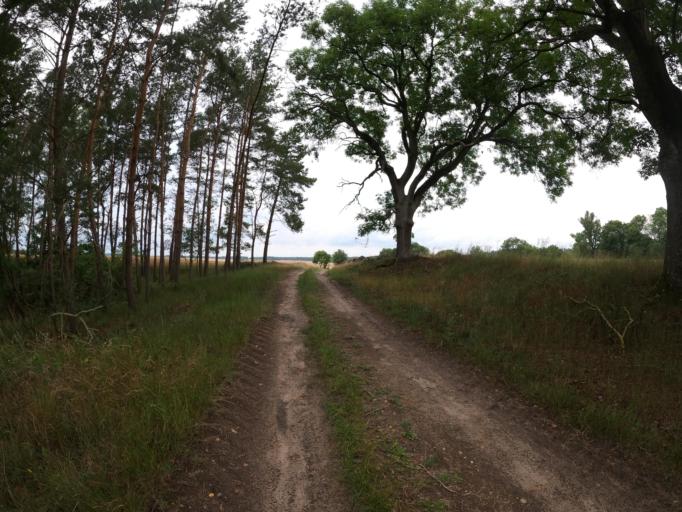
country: DE
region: Brandenburg
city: Althuttendorf
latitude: 53.0273
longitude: 13.8905
